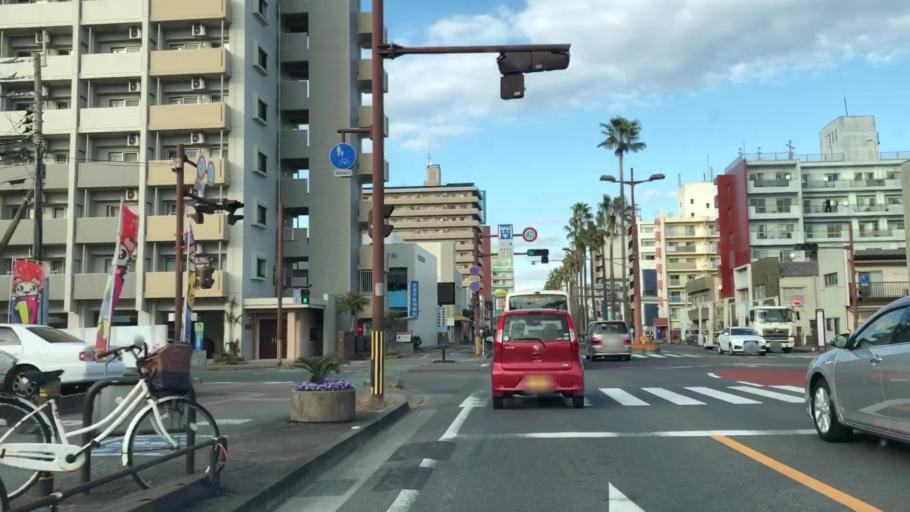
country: JP
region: Miyazaki
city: Miyazaki-shi
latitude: 31.9010
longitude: 131.4187
